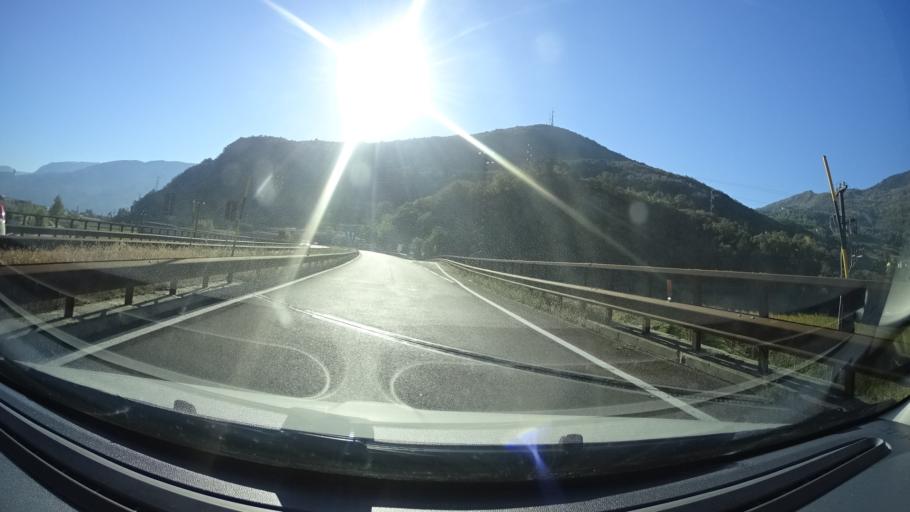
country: IT
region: Trentino-Alto Adige
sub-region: Provincia di Trento
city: Mori
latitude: 45.8525
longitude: 10.9595
